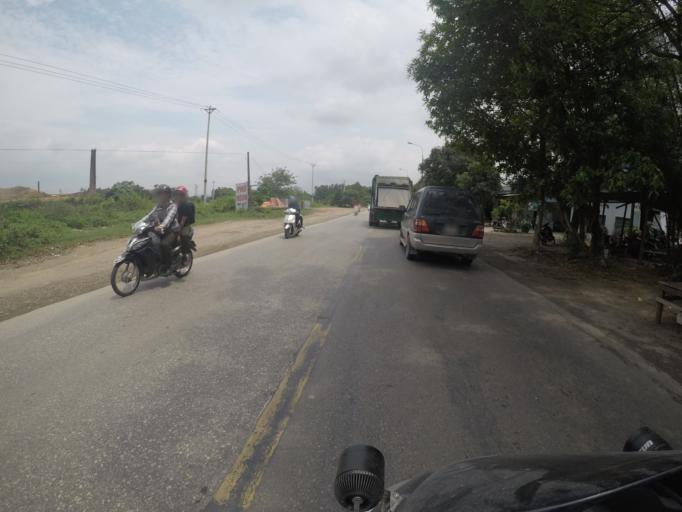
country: VN
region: Ha Noi
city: Soc Son
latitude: 21.2208
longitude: 105.8490
